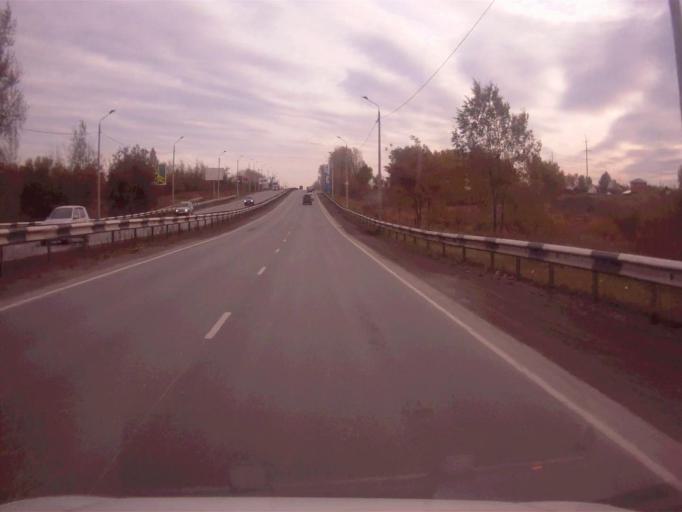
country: RU
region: Chelyabinsk
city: Novosineglazovskiy
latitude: 55.0583
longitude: 61.4042
